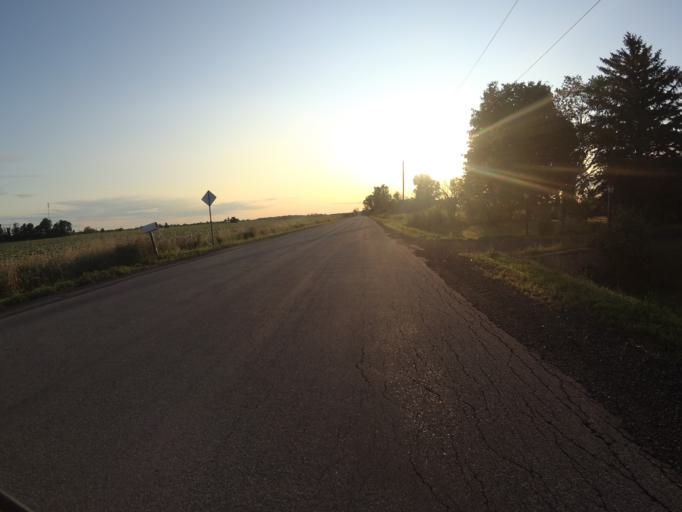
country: CA
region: Ontario
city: Ottawa
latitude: 45.1280
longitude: -75.4919
